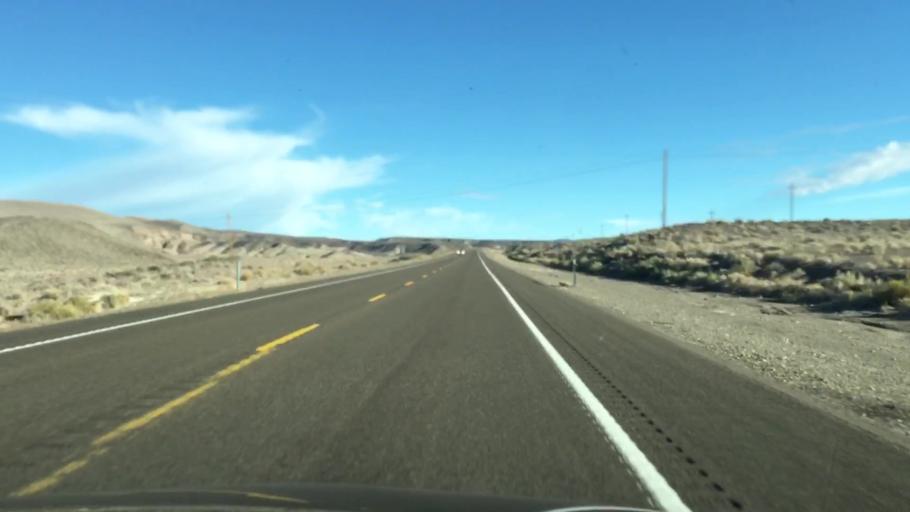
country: US
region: Nevada
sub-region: Mineral County
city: Hawthorne
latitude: 38.2382
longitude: -118.0338
